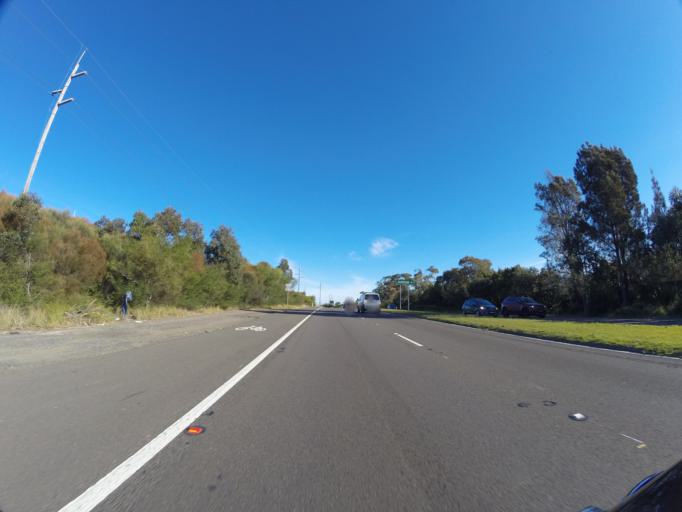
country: AU
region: New South Wales
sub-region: Sutherland Shire
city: Heathcote
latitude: -34.0950
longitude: 151.0001
